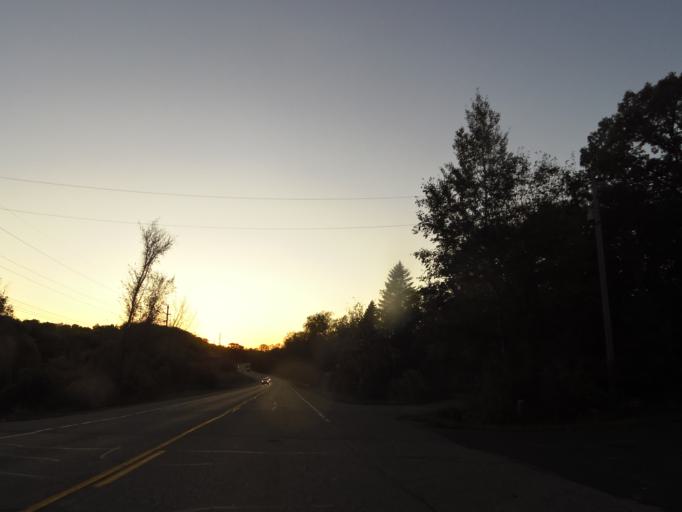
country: US
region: Minnesota
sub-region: Dakota County
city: Eagan
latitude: 44.7902
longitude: -93.1298
